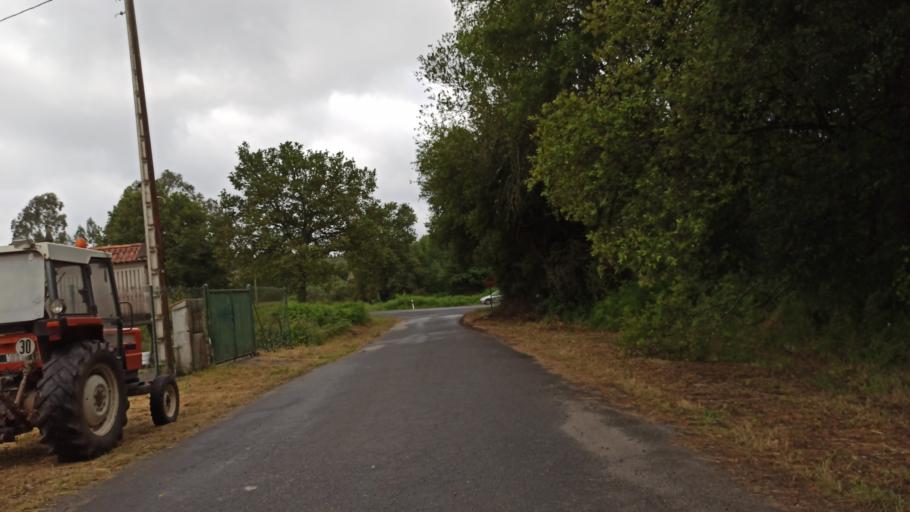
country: ES
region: Galicia
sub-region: Provincia da Coruna
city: Santiso
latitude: 42.7626
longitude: -8.0272
